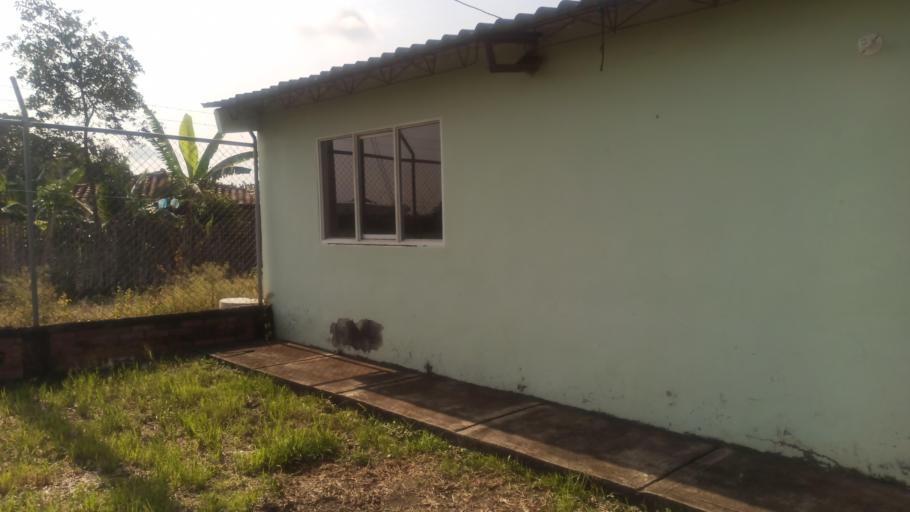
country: CO
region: Valle del Cauca
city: Jamundi
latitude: 3.1416
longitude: -76.5469
